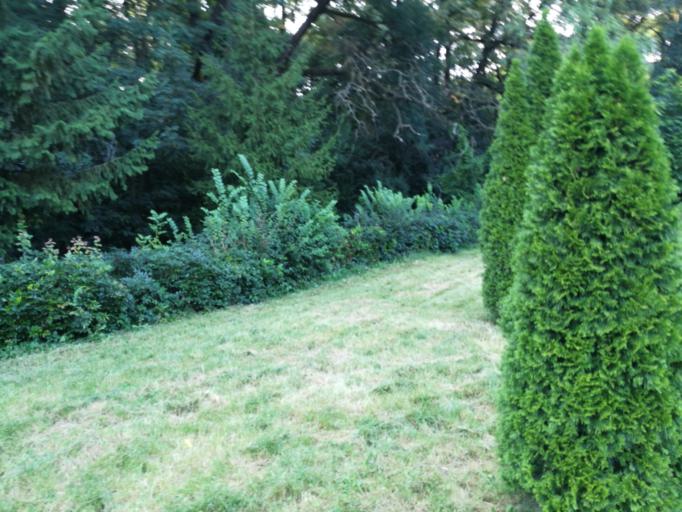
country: RO
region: Ilfov
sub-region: Comuna Otopeni
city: Otopeni
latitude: 44.5194
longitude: 26.0903
